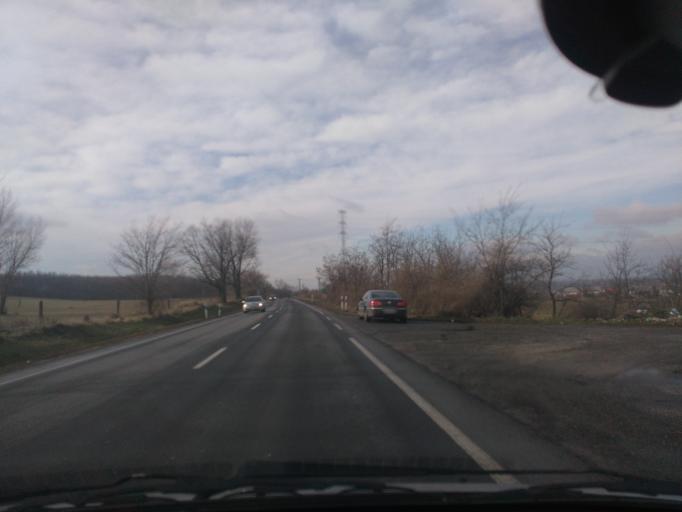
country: HU
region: Komarom-Esztergom
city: Dorog
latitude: 47.7296
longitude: 18.7037
